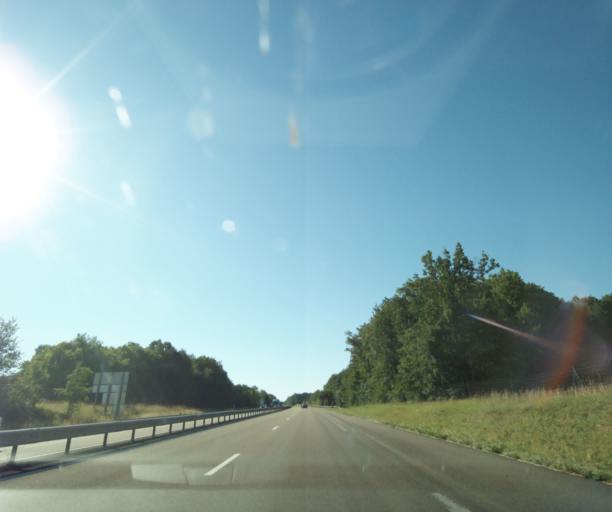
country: FR
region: Champagne-Ardenne
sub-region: Departement de l'Aube
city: Lusigny-sur-Barse
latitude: 48.2021
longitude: 4.2573
